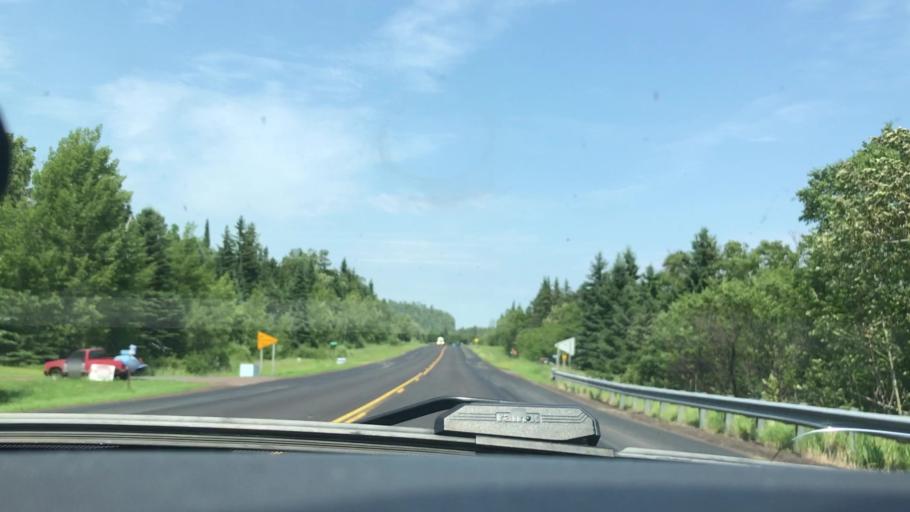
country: US
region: Minnesota
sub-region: Lake County
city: Silver Bay
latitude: 47.3580
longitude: -91.1783
